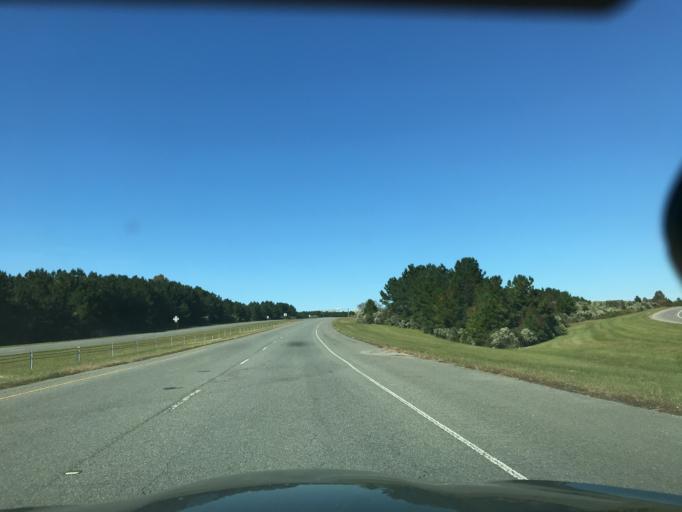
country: US
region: North Carolina
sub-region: Wake County
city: Morrisville
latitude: 35.8867
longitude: -78.8119
